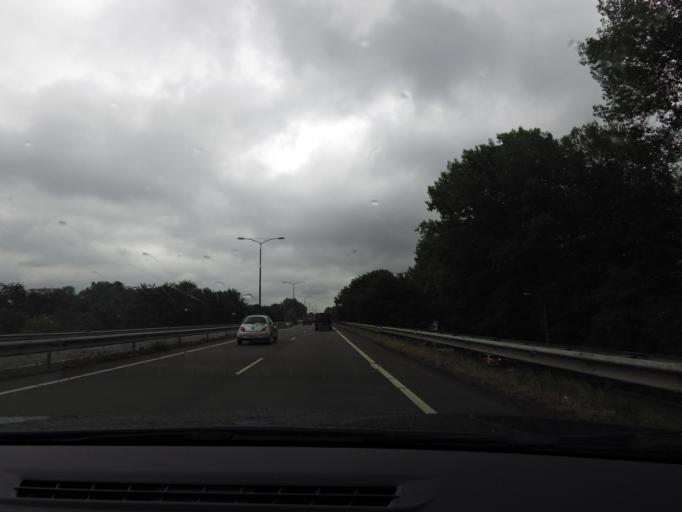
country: NL
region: South Holland
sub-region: Gemeente Delft
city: Delft
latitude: 51.9908
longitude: 4.3663
